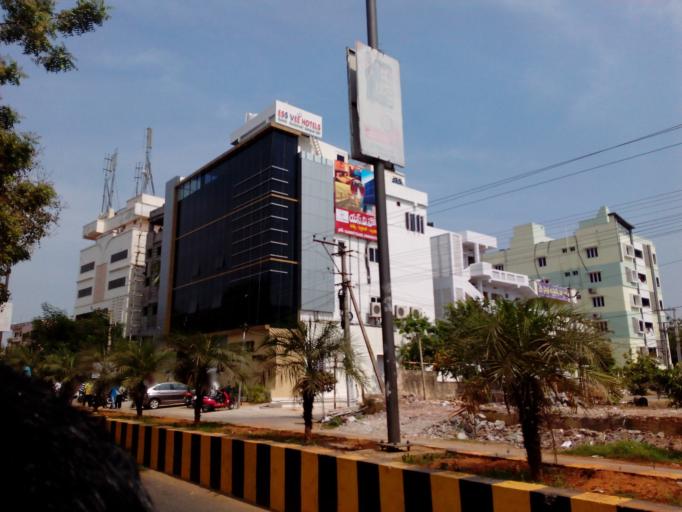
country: IN
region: Andhra Pradesh
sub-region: Krishna
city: Yanamalakuduru
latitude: 16.5087
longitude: 80.6621
